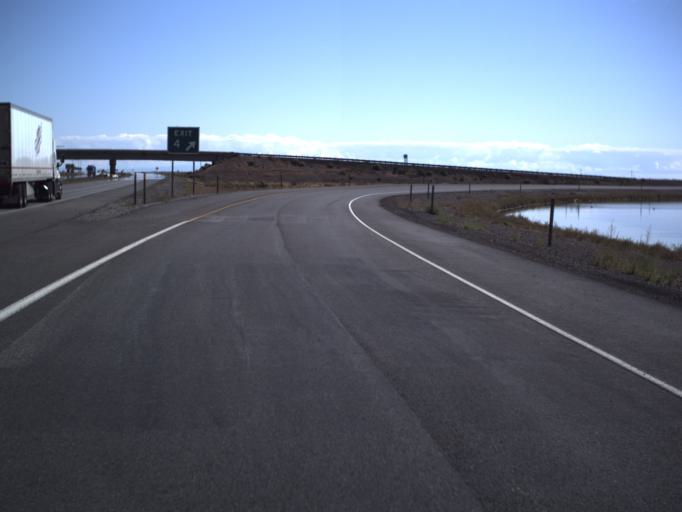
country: US
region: Utah
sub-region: Tooele County
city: Wendover
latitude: 40.7425
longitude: -113.9753
